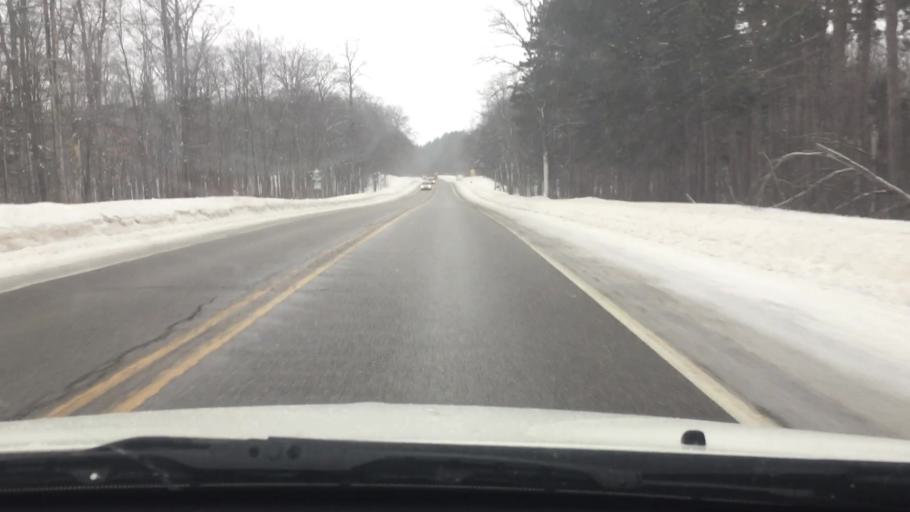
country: US
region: Michigan
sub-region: Otsego County
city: Gaylord
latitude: 45.0603
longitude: -84.7950
